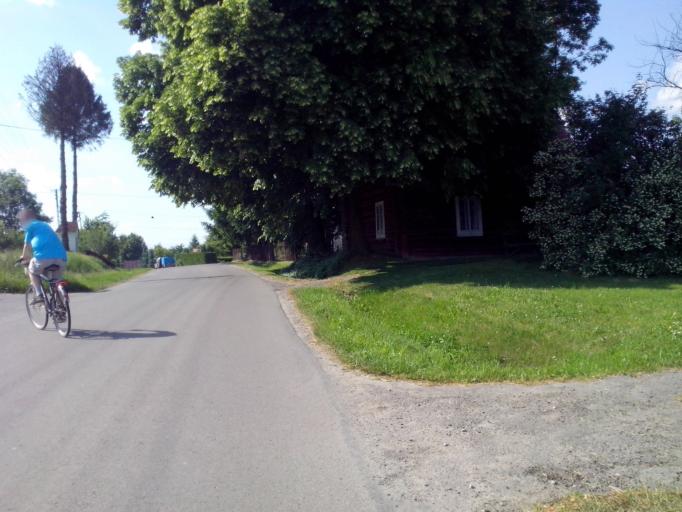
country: PL
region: Subcarpathian Voivodeship
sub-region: Powiat brzozowski
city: Blizne
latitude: 49.7330
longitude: 21.9846
